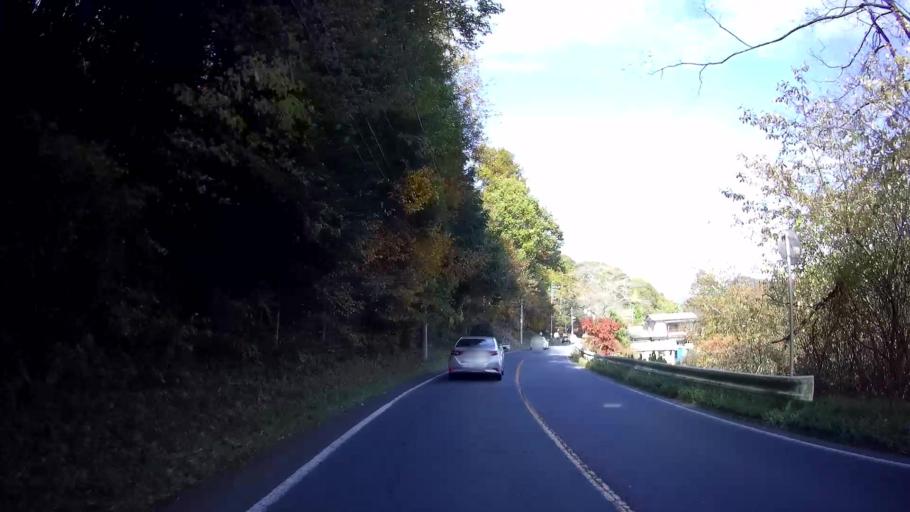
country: JP
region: Gunma
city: Nakanojomachi
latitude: 36.5001
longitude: 138.7767
